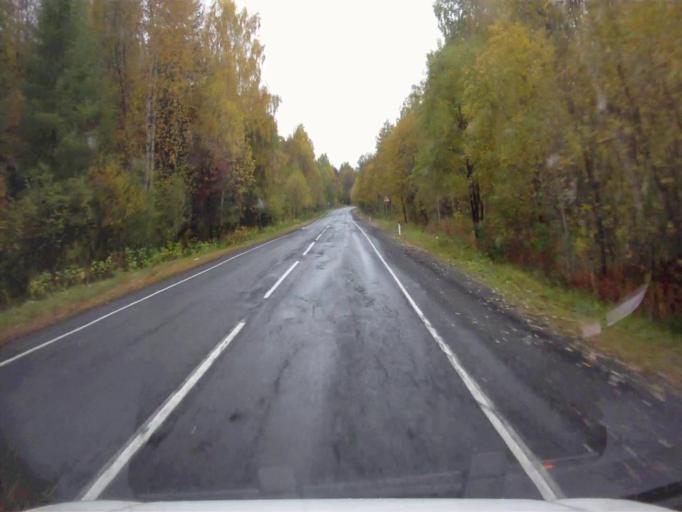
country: RU
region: Chelyabinsk
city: Verkhniy Ufaley
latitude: 56.0431
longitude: 60.1018
